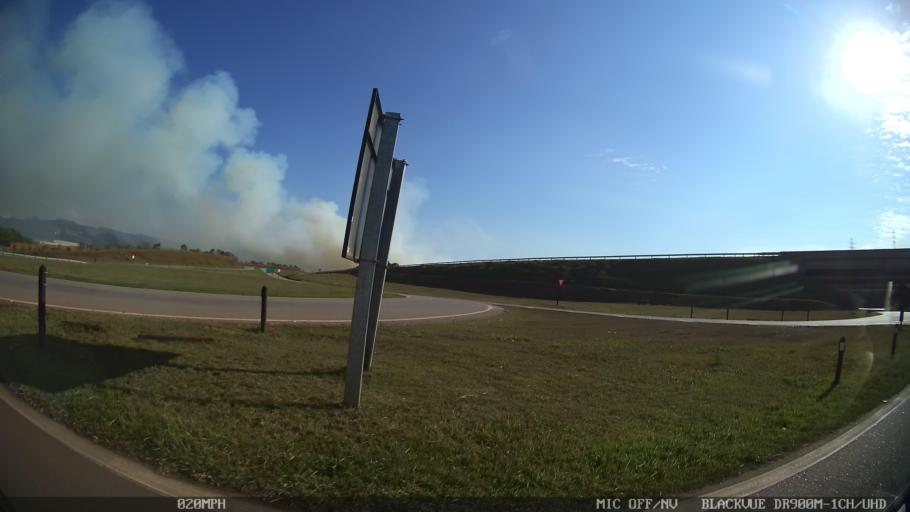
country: BR
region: Sao Paulo
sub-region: Piracicaba
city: Piracicaba
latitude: -22.6927
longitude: -47.5997
